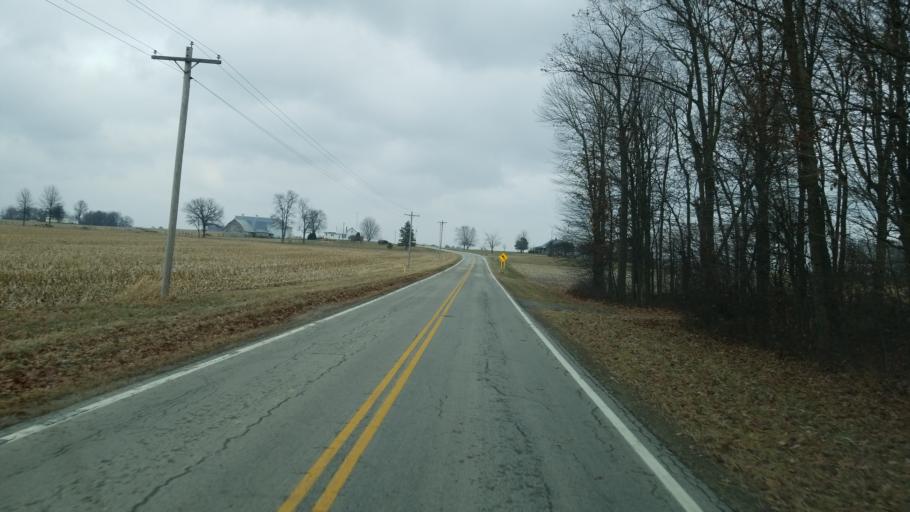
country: US
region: Ohio
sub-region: Wyandot County
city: Upper Sandusky
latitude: 40.7386
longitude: -83.2012
